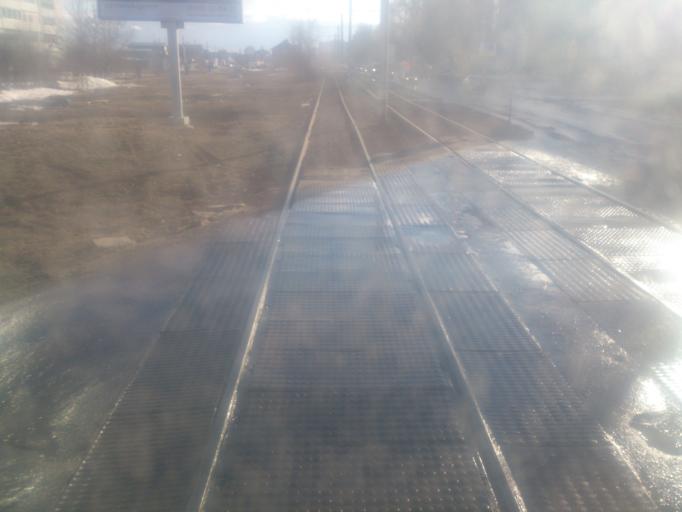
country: RU
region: Ulyanovsk
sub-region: Ulyanovskiy Rayon
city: Ulyanovsk
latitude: 54.2692
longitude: 48.2851
